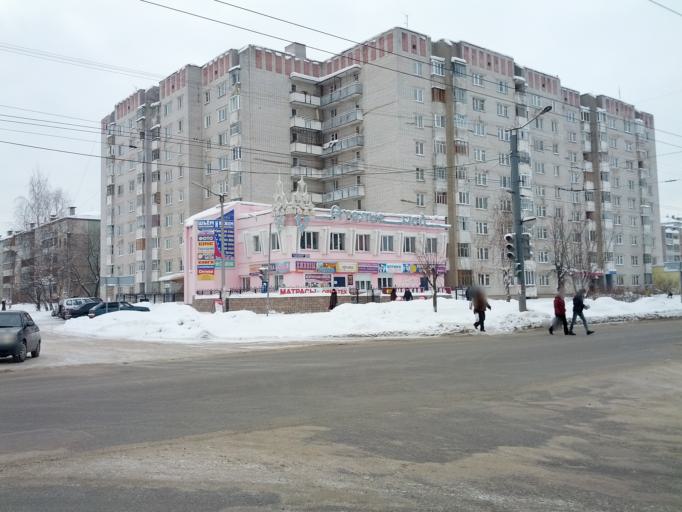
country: RU
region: Mariy-El
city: Yoshkar-Ola
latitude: 56.6465
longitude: 47.8651
